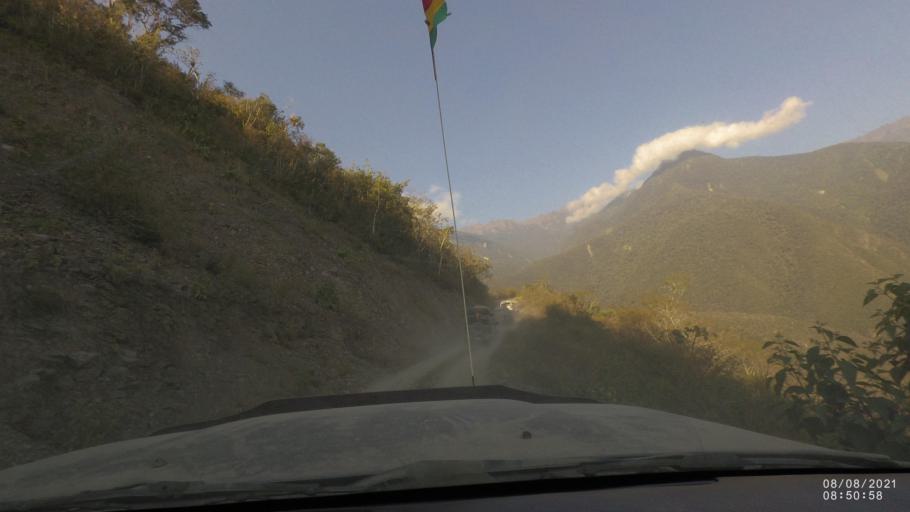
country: BO
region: La Paz
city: Quime
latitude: -16.5366
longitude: -66.7601
